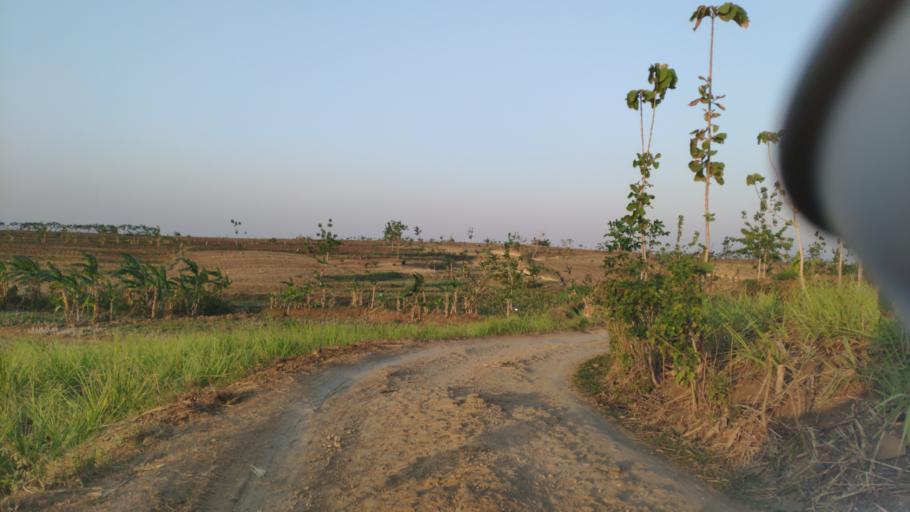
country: ID
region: Central Java
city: Jepang
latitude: -7.0259
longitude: 111.2358
